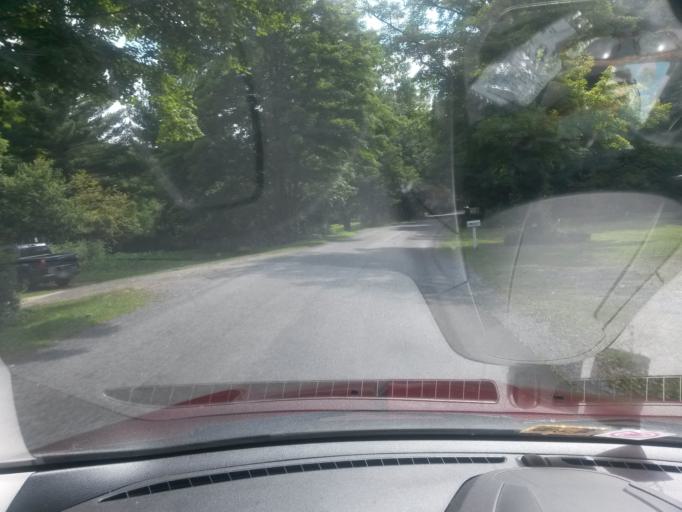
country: US
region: Virginia
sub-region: Bath County
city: Warm Springs
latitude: 37.9276
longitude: -79.7808
